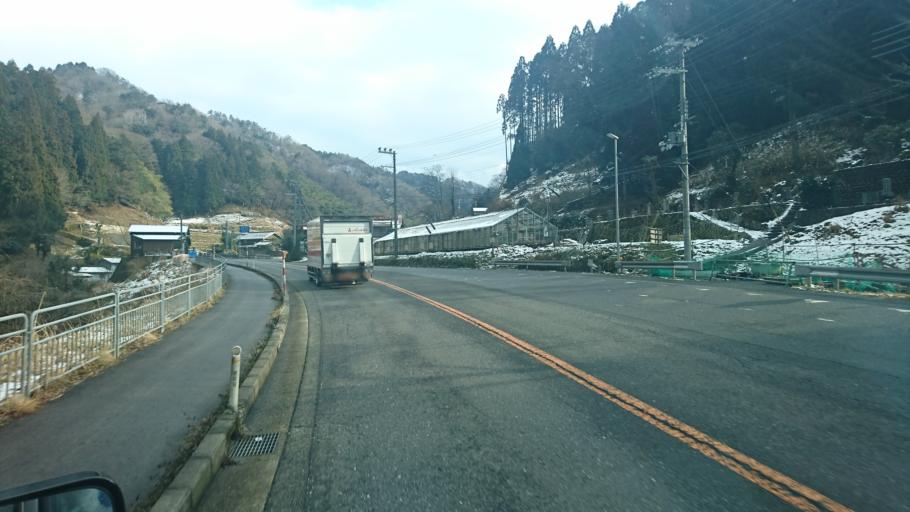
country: JP
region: Tottori
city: Tottori
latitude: 35.5253
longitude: 134.5194
